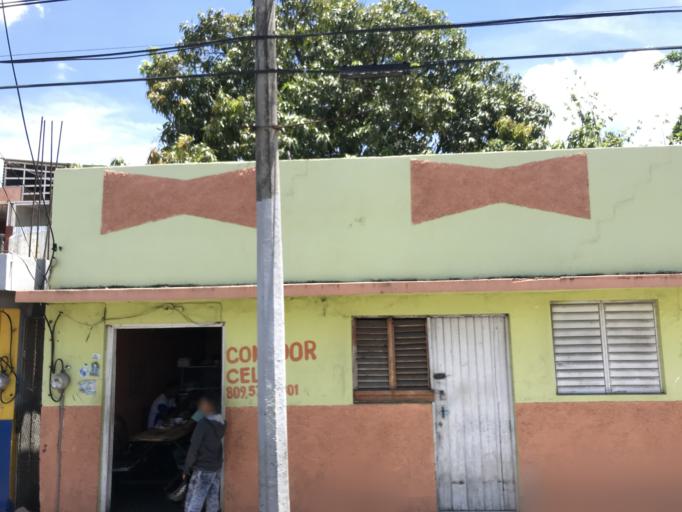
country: DO
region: Santiago
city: Santiago de los Caballeros
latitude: 19.4869
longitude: -70.7258
